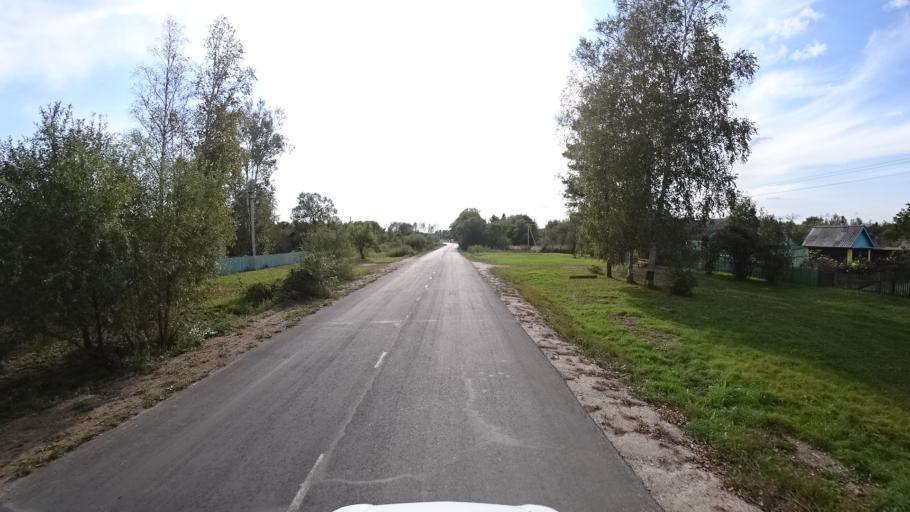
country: RU
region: Amur
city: Arkhara
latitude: 49.3657
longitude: 130.1275
